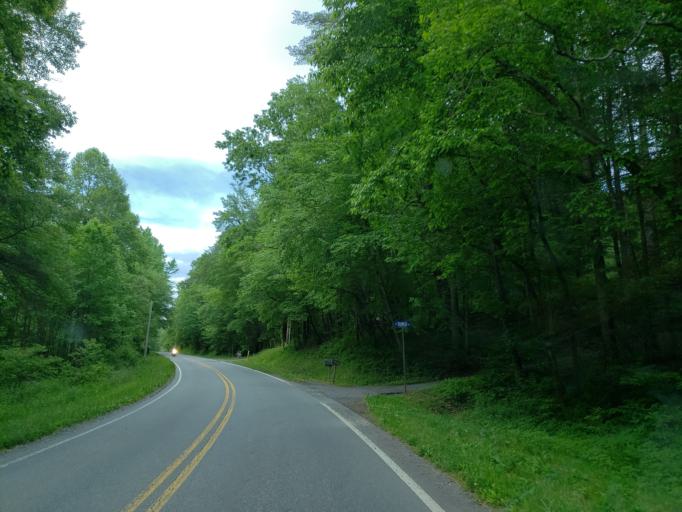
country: US
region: Georgia
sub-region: Fannin County
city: Blue Ridge
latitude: 34.8460
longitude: -84.3929
